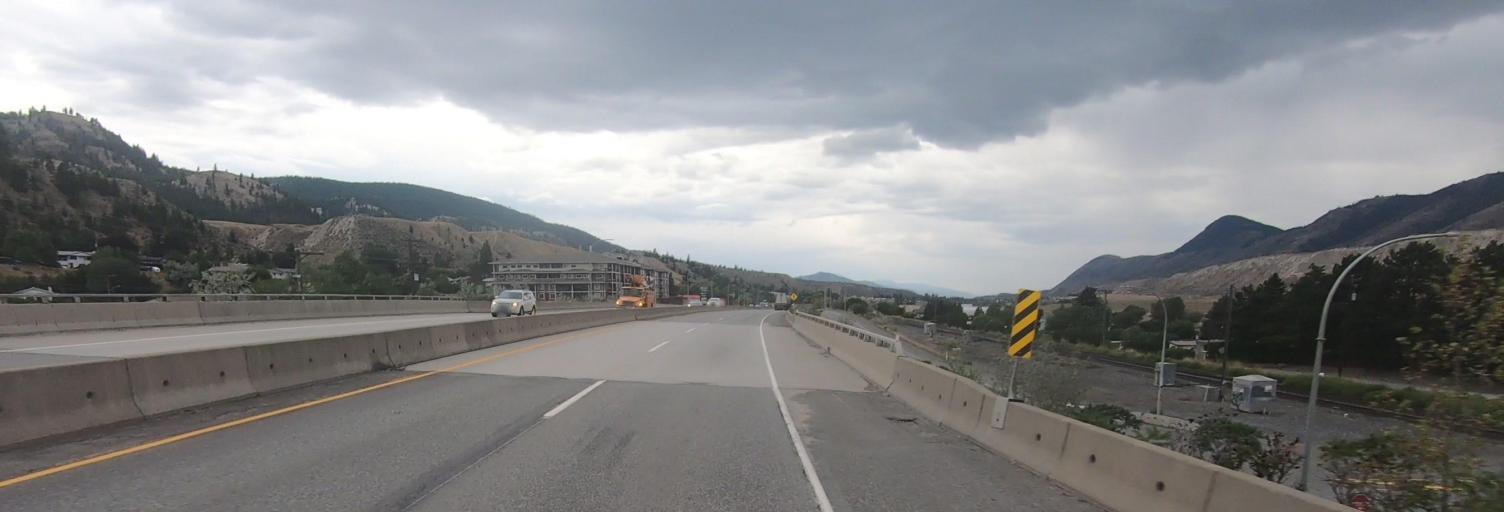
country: CA
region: British Columbia
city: Kamloops
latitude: 50.6698
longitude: -120.1811
